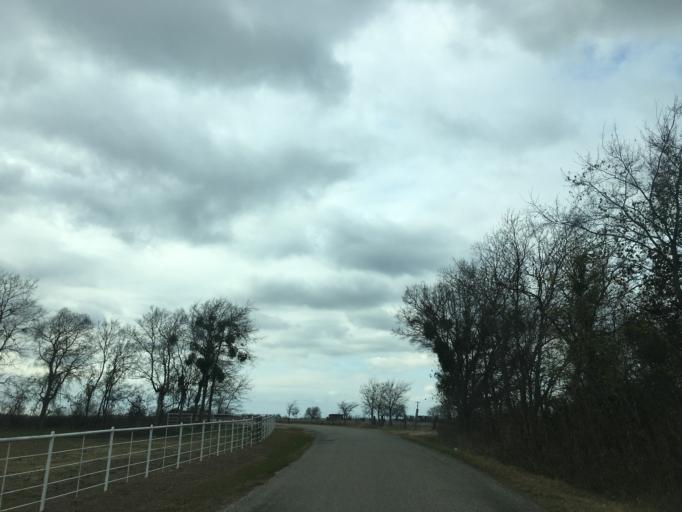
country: US
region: Texas
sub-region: Ellis County
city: Palmer
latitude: 32.4640
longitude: -96.6459
